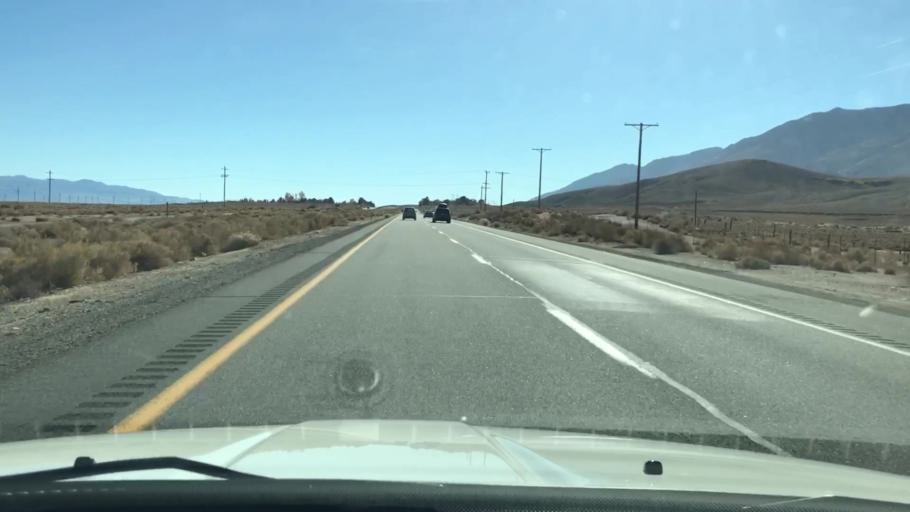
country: US
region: California
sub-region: Inyo County
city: Lone Pine
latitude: 36.5559
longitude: -118.0500
